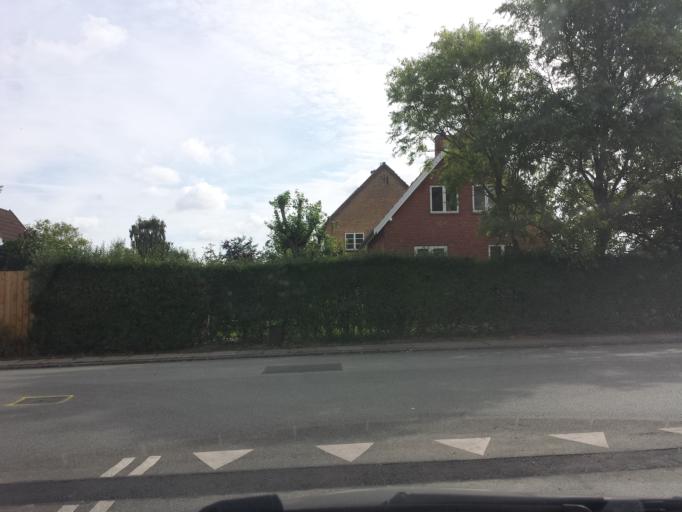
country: DK
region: Capital Region
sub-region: Rodovre Kommune
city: Rodovre
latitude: 55.6797
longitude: 12.4594
